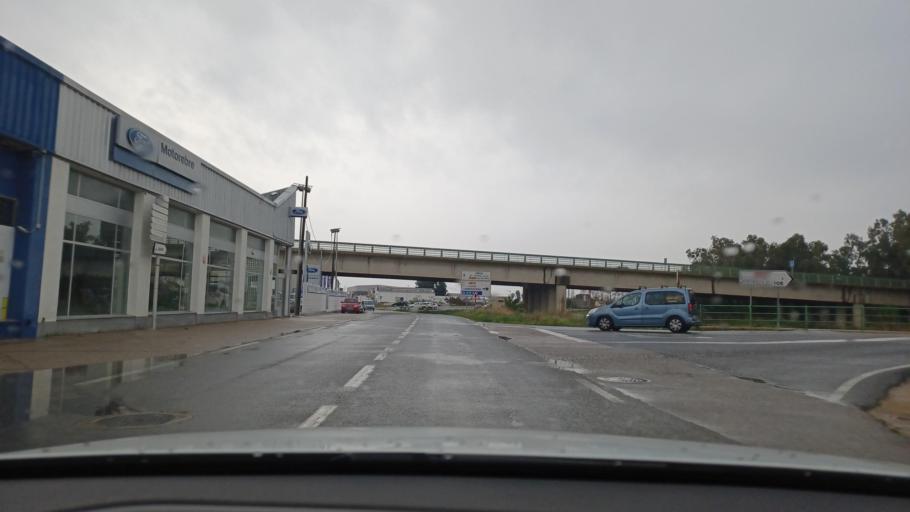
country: ES
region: Catalonia
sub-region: Provincia de Tarragona
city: Amposta
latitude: 40.7084
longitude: 0.5890
